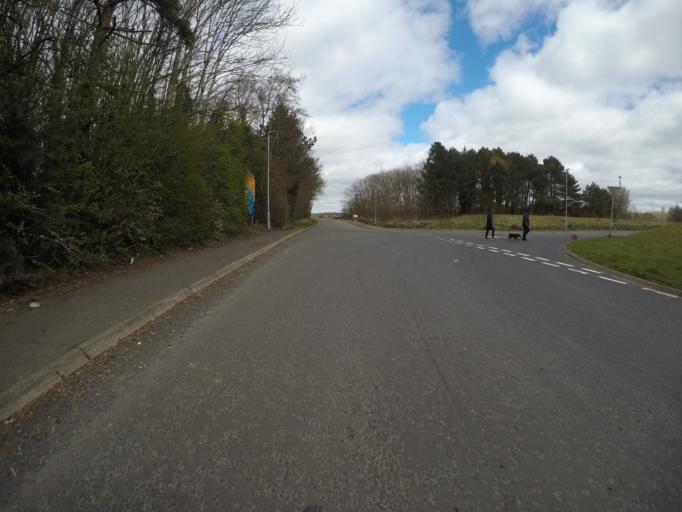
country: GB
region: Scotland
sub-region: North Ayrshire
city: Irvine
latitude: 55.6173
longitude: -4.6450
